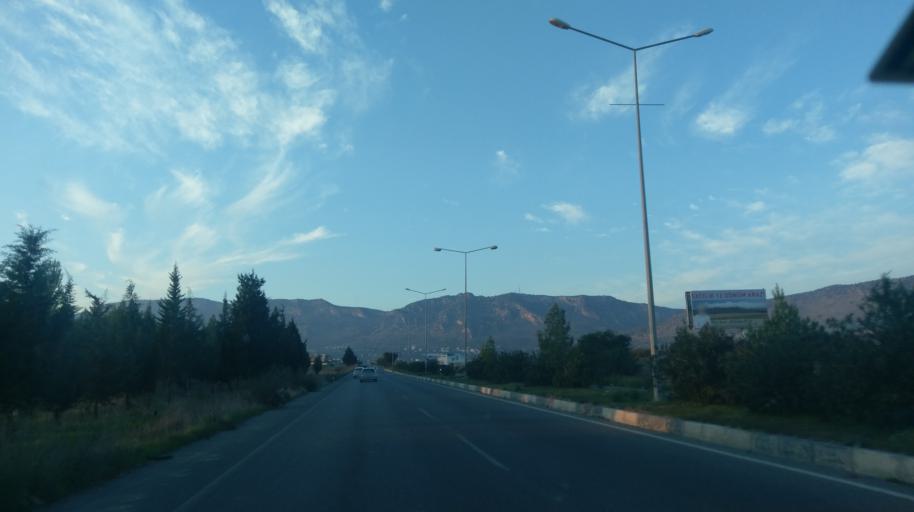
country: CY
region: Keryneia
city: Kyrenia
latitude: 35.2636
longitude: 33.2949
